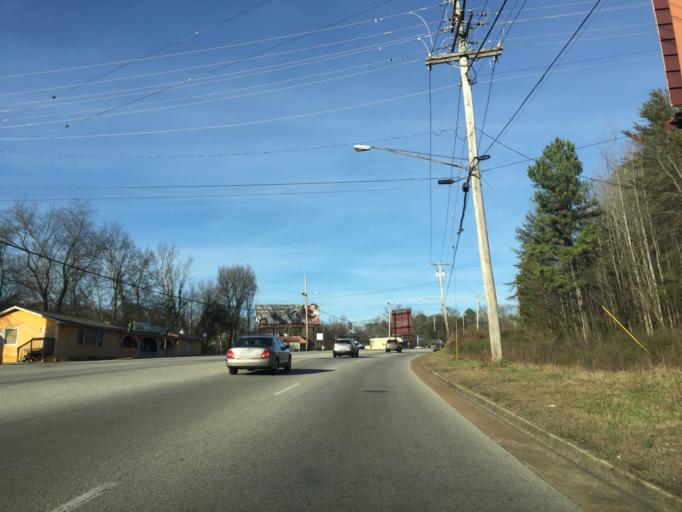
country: US
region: Tennessee
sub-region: Hamilton County
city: Red Bank
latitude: 35.1098
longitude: -85.2710
